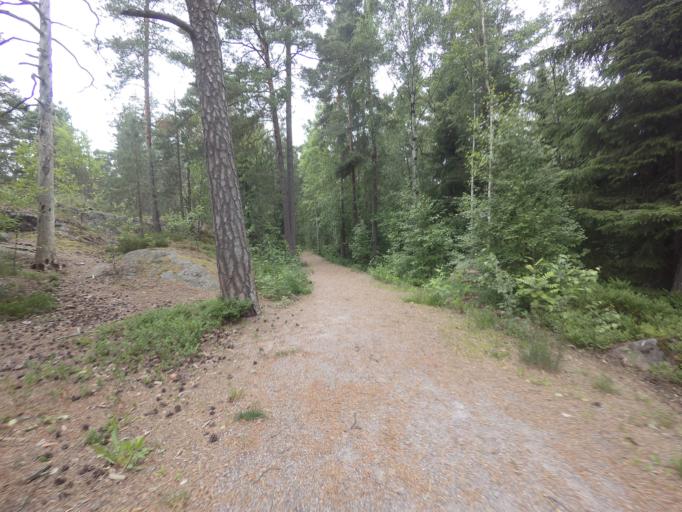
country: FI
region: Uusimaa
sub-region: Helsinki
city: Koukkuniemi
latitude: 60.1769
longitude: 24.7446
